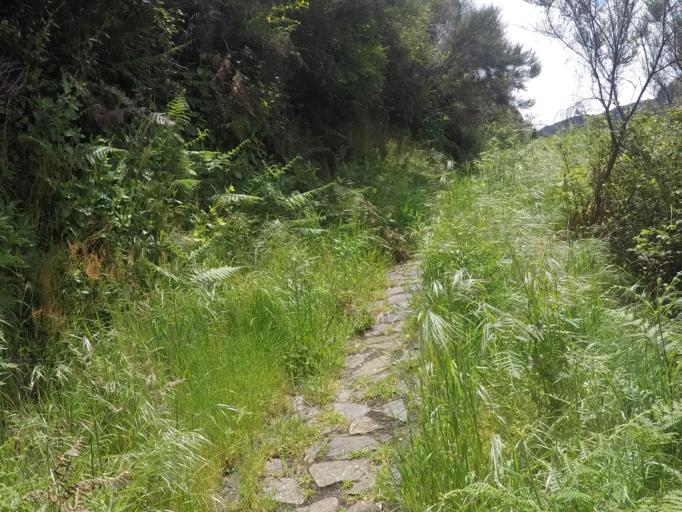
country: PT
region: Madeira
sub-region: Camara de Lobos
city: Curral das Freiras
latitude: 32.7406
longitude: -17.0035
